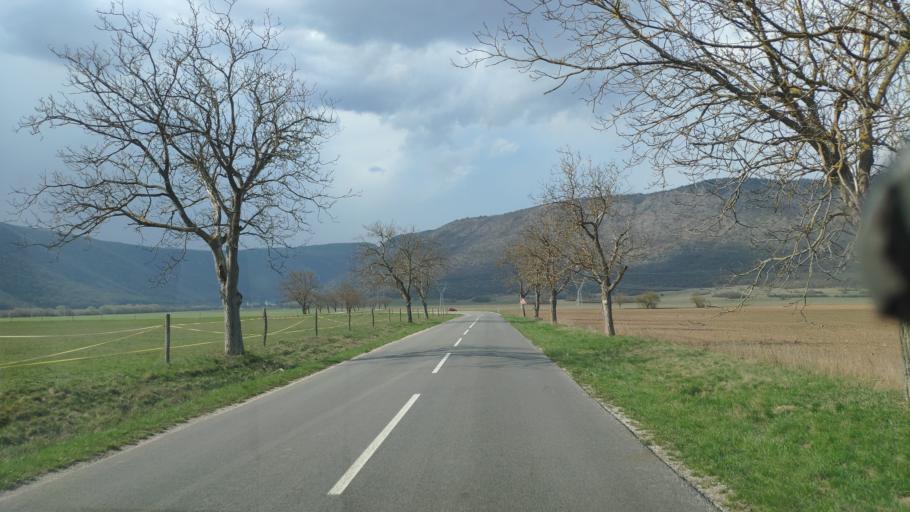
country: SK
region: Kosicky
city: Medzev
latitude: 48.6136
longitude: 20.8825
